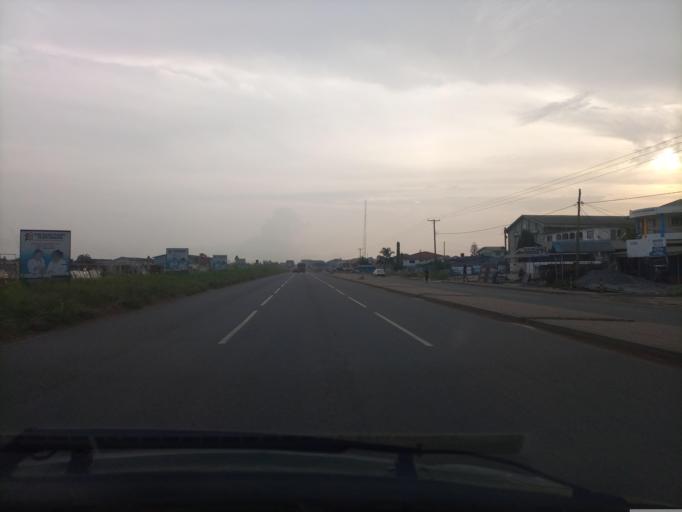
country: GH
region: Western
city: Takoradi
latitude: 4.9270
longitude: -1.7823
